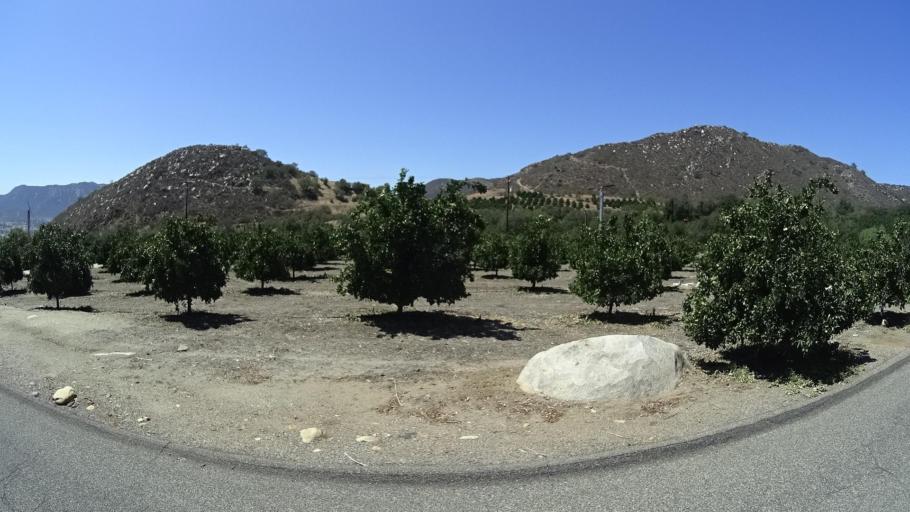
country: US
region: California
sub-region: San Diego County
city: Rainbow
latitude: 33.3813
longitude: -117.0450
